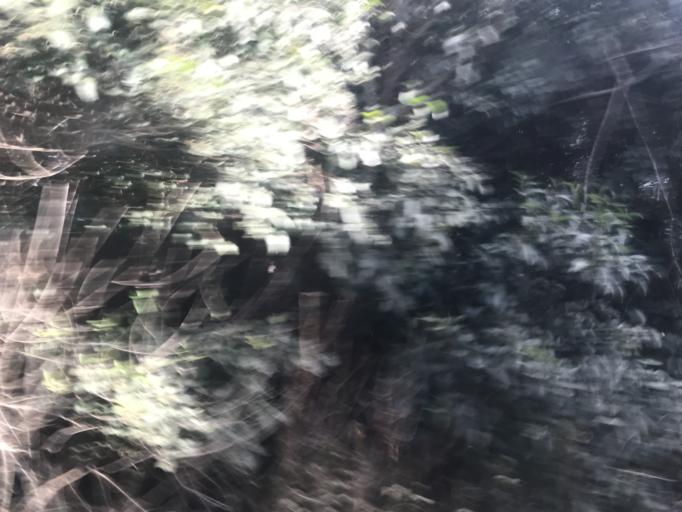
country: AR
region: Cordoba
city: Laguna Larga
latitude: -31.7994
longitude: -63.7835
